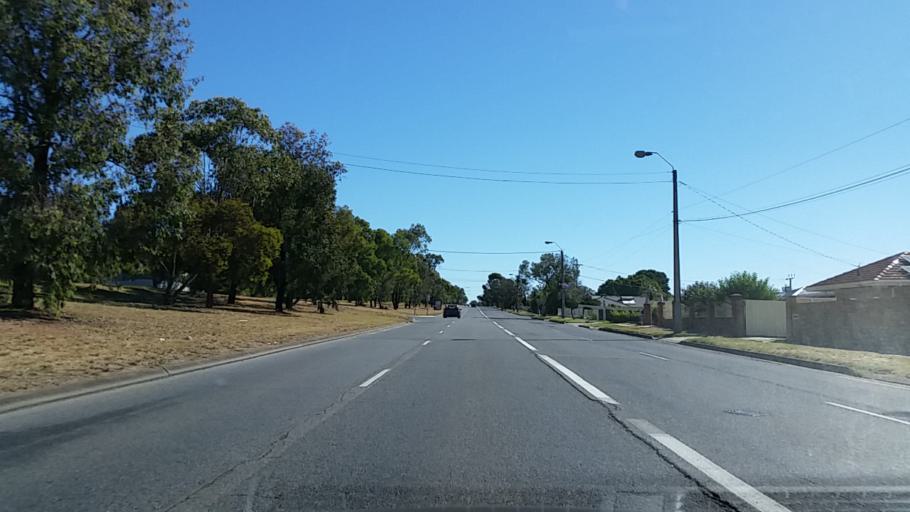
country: AU
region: South Australia
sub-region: Salisbury
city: Ingle Farm
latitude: -34.8293
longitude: 138.6312
